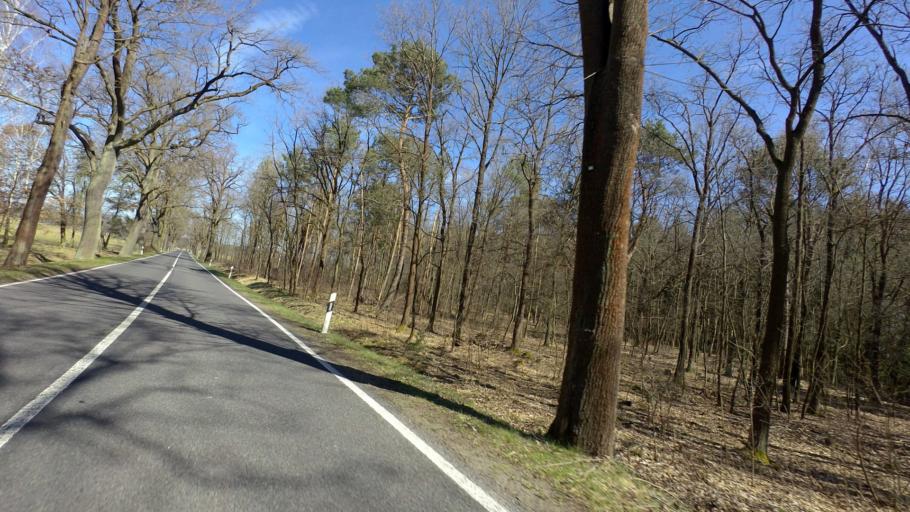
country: DE
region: Brandenburg
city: Munchehofe
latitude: 52.1345
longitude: 13.8267
